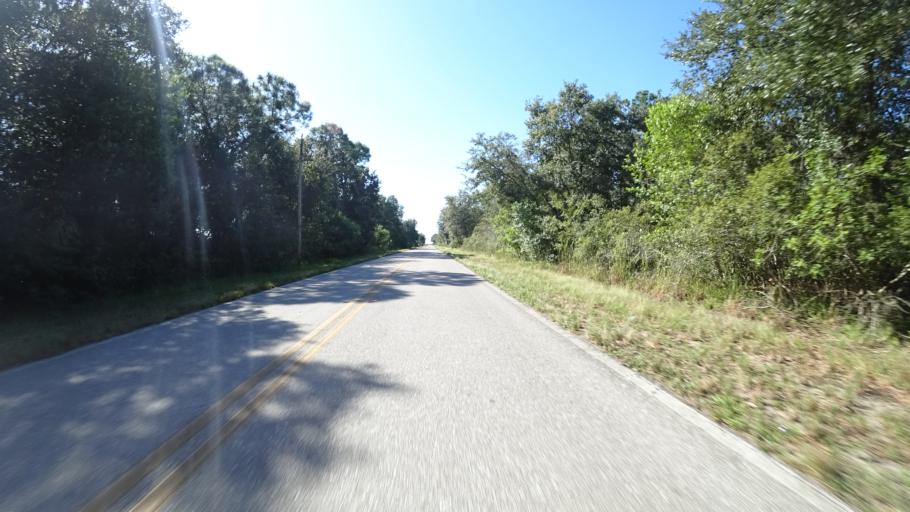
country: US
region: Florida
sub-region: Hillsborough County
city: Wimauma
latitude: 27.6263
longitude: -82.2925
